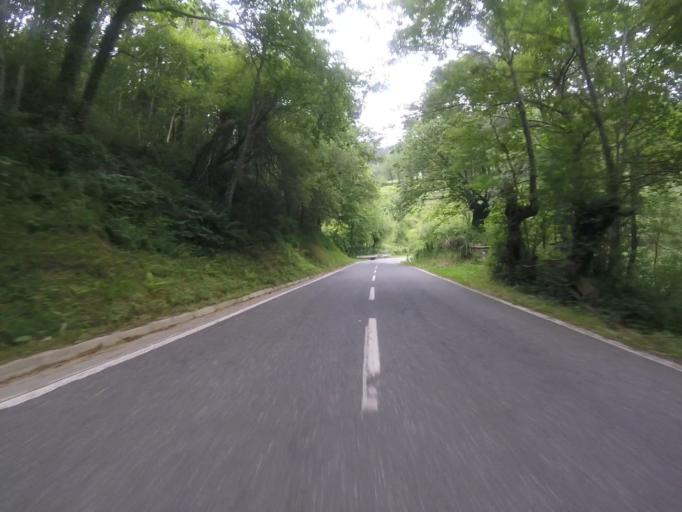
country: ES
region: Navarre
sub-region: Provincia de Navarra
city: Ezkurra
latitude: 43.0844
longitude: -1.8332
